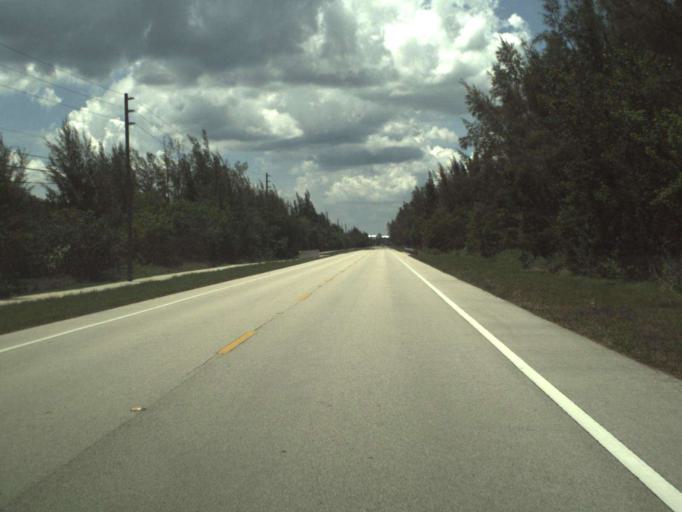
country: US
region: Florida
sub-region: Saint Lucie County
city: Indian River Estates
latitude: 27.4032
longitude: -80.2683
